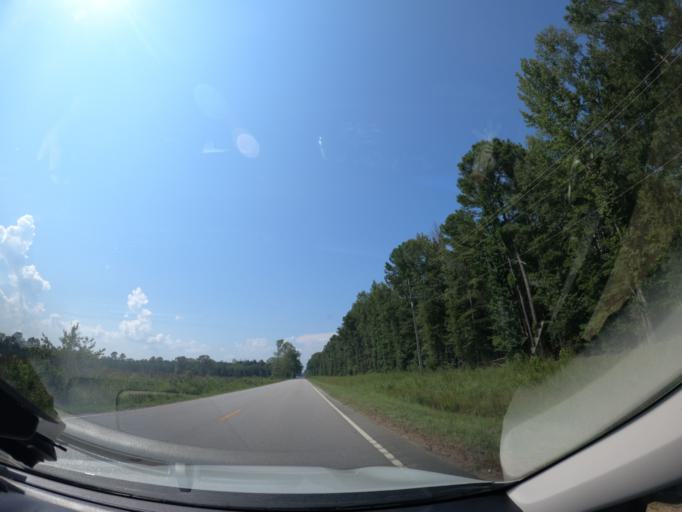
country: US
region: South Carolina
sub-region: Richland County
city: Hopkins
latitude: 33.8807
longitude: -80.9039
